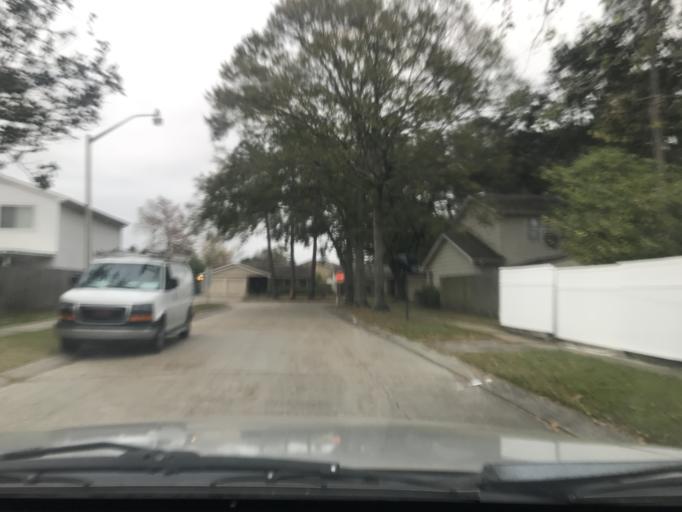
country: US
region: Louisiana
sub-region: Jefferson Parish
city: Woodmere
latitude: 29.8624
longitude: -90.0801
